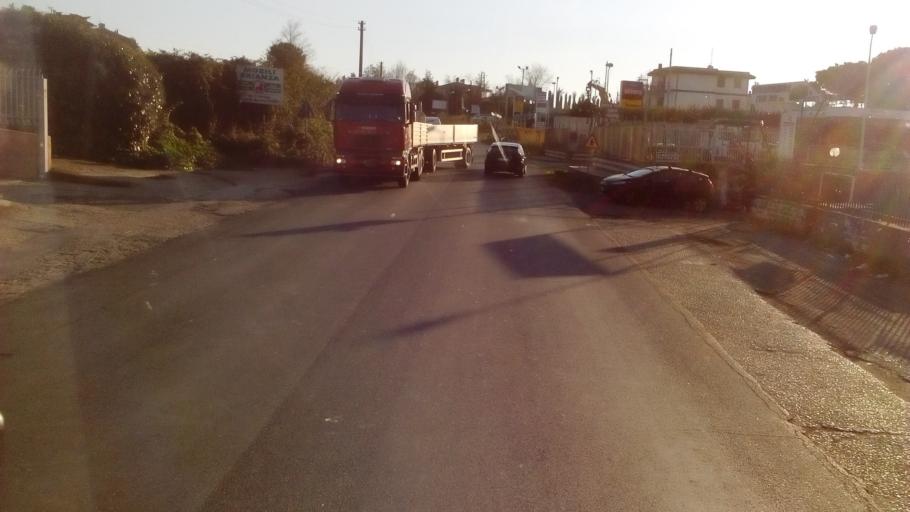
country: IT
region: Latium
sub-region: Citta metropolitana di Roma Capitale
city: Pavona
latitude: 41.7391
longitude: 12.6163
